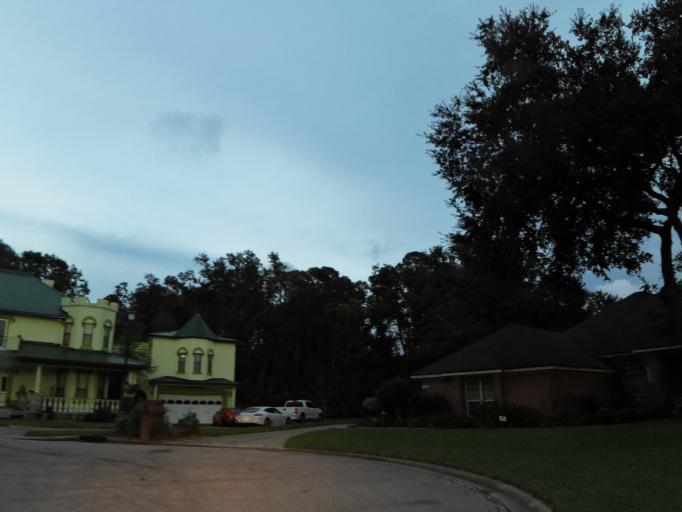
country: US
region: Florida
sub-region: Duval County
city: Jacksonville
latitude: 30.3841
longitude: -81.6200
